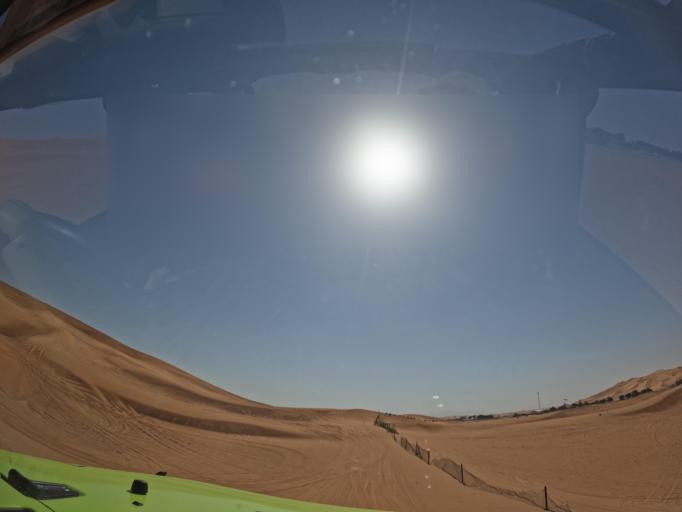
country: AE
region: Ash Shariqah
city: Adh Dhayd
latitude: 24.9589
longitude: 55.7163
